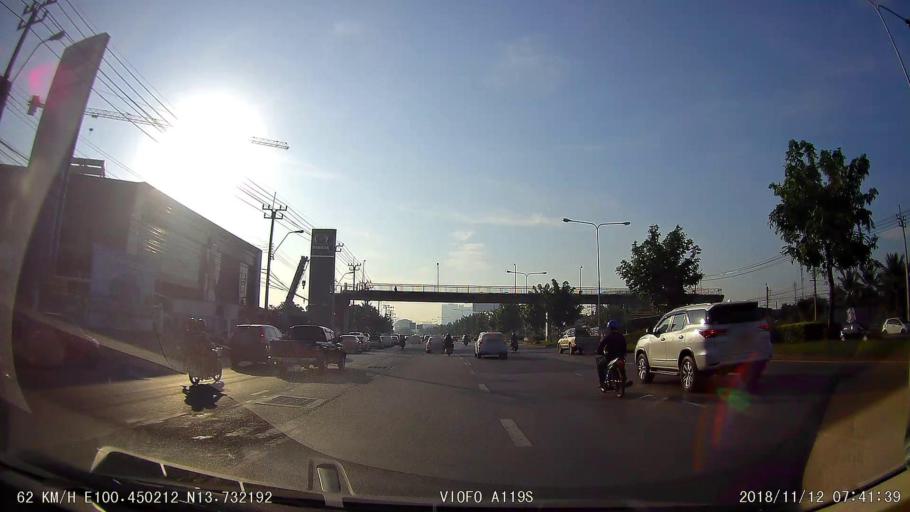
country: TH
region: Bangkok
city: Phasi Charoen
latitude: 13.7323
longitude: 100.4502
